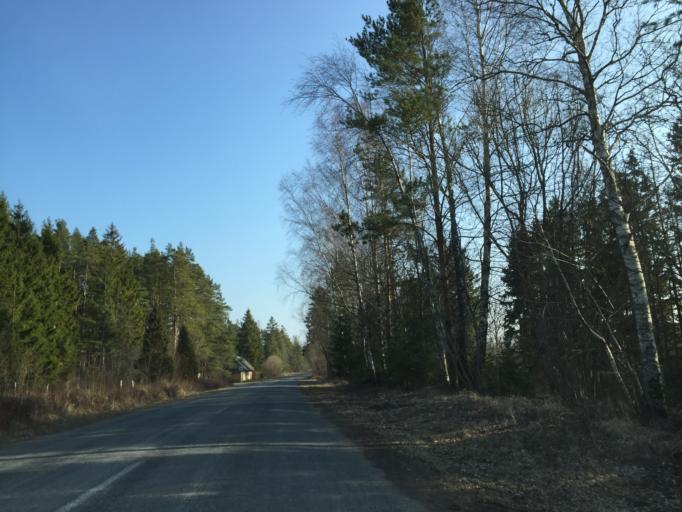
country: EE
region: Saare
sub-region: Orissaare vald
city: Orissaare
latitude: 58.6059
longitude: 23.3126
